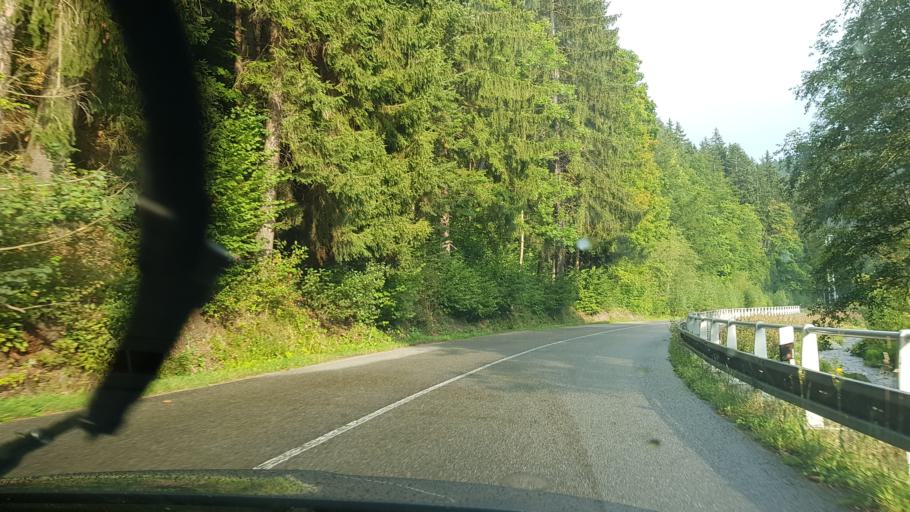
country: CZ
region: Olomoucky
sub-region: Okres Sumperk
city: Hanusovice
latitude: 50.0893
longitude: 16.9042
